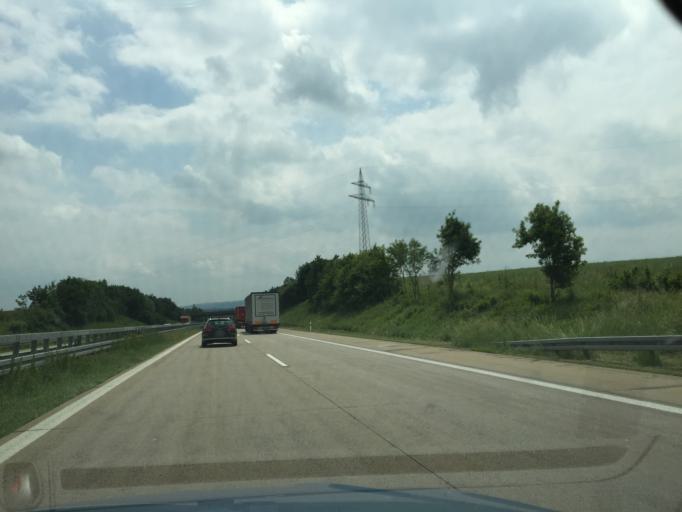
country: DE
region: Baden-Wuerttemberg
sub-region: Regierungsbezirk Stuttgart
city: Westhausen
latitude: 48.9363
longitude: 10.1937
